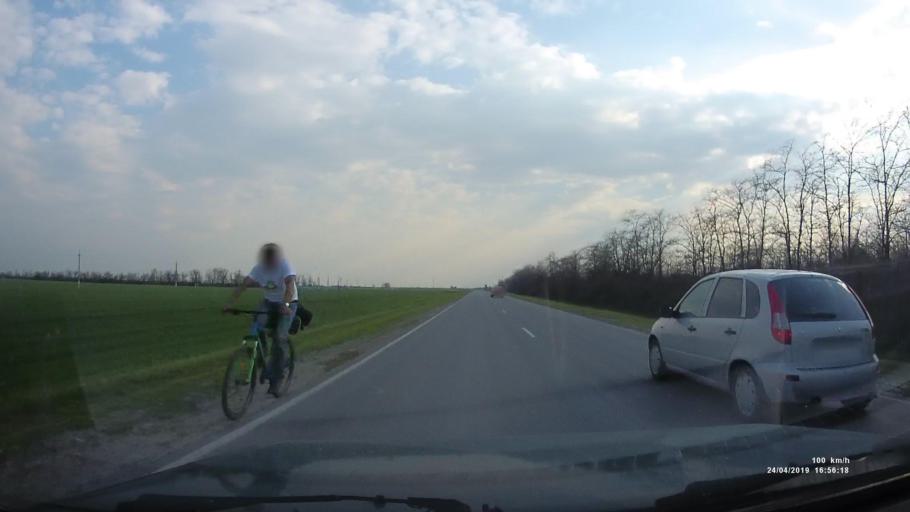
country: RU
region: Rostov
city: Proletarsk
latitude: 46.6534
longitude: 41.6797
